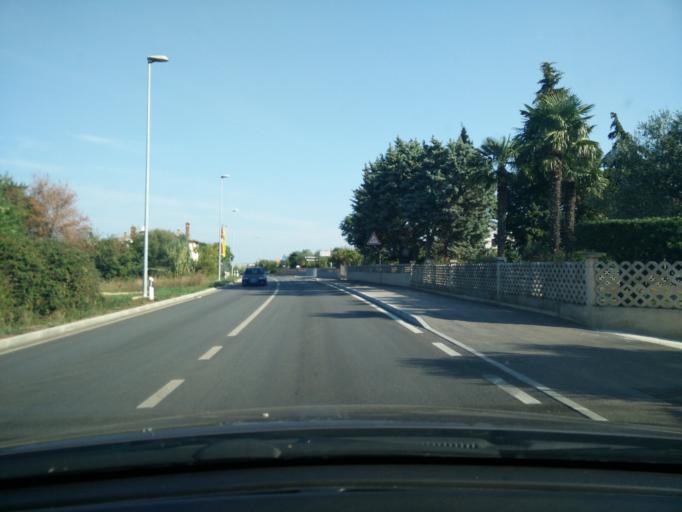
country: HR
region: Istarska
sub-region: Grad Porec
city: Porec
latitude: 45.2498
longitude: 13.6124
